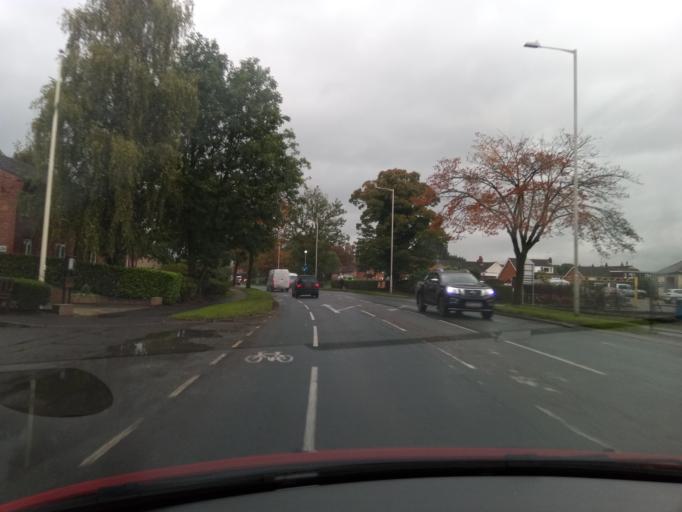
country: GB
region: England
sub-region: Lancashire
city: Catterall
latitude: 53.8535
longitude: -2.7449
